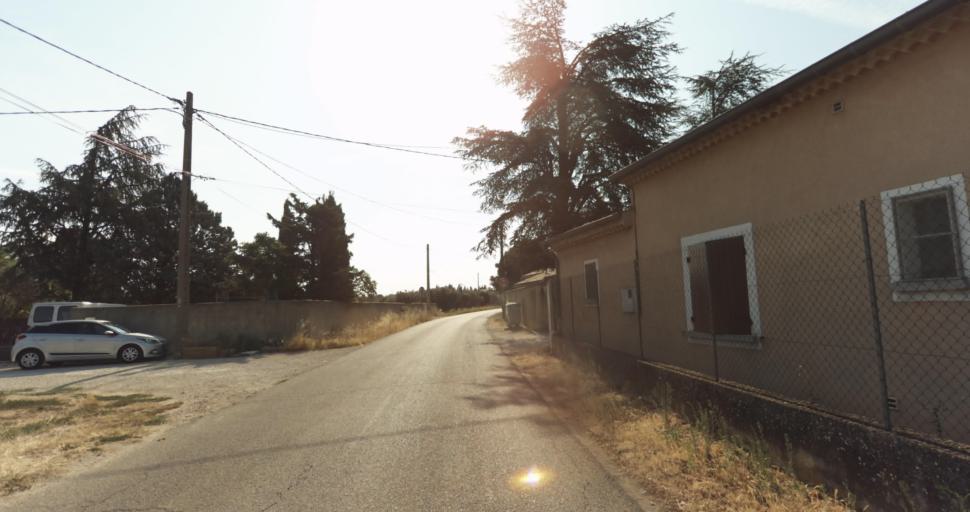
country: FR
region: Provence-Alpes-Cote d'Azur
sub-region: Departement du Vaucluse
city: Monteux
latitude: 44.0361
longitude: 5.0196
